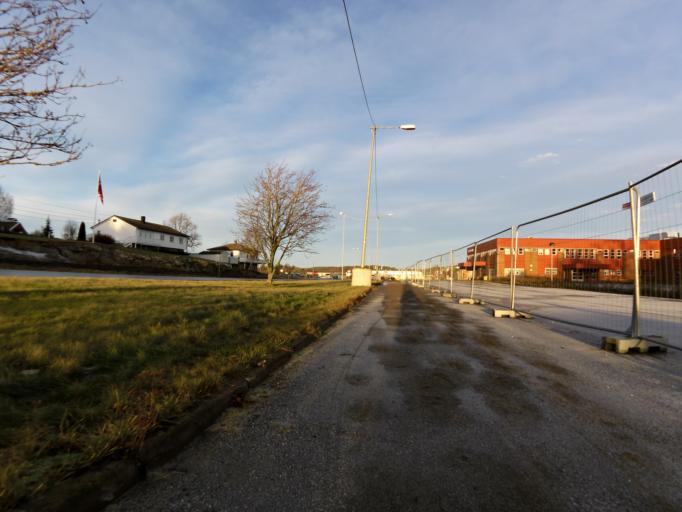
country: NO
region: Ostfold
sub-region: Fredrikstad
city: Fredrikstad
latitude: 59.2321
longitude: 10.9039
